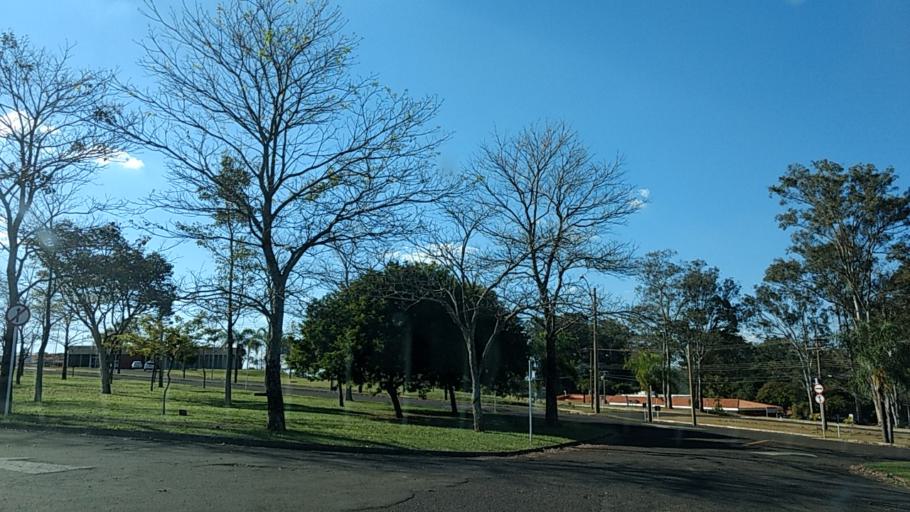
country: BR
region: Sao Paulo
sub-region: Botucatu
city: Botucatu
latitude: -22.8518
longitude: -48.4338
